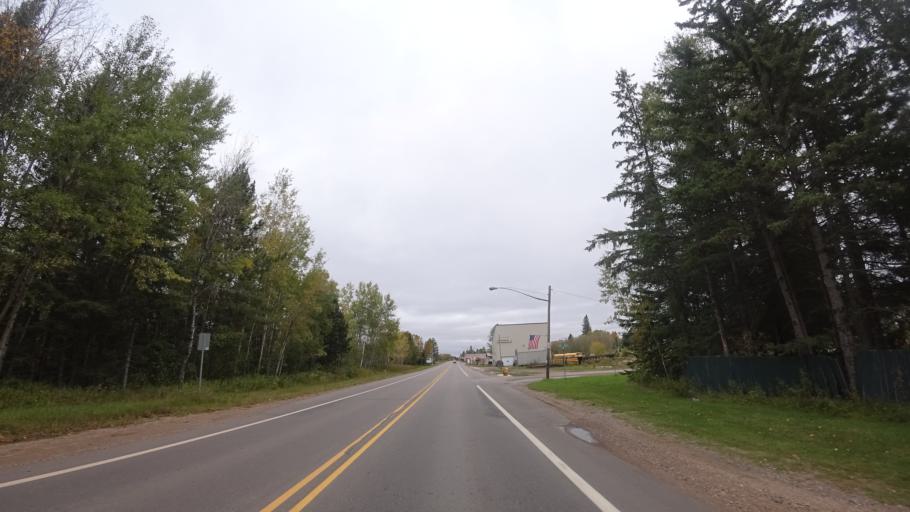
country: US
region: Michigan
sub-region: Iron County
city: Crystal Falls
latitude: 46.1377
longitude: -88.0933
